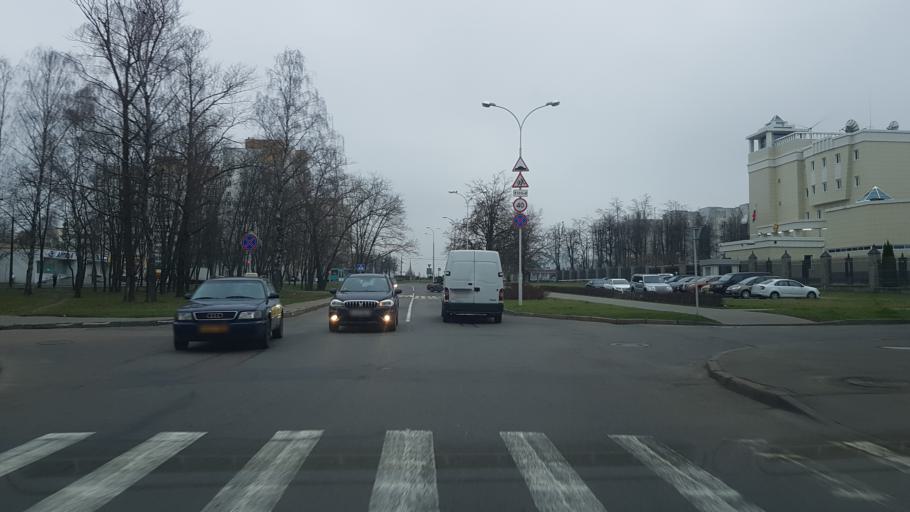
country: BY
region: Minsk
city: Minsk
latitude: 53.9273
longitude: 27.5435
